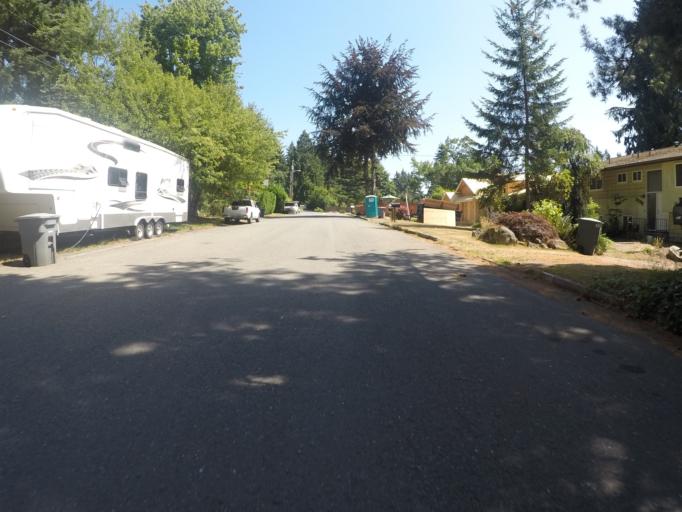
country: US
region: Washington
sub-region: King County
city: Kenmore
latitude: 47.7760
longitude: -122.2375
